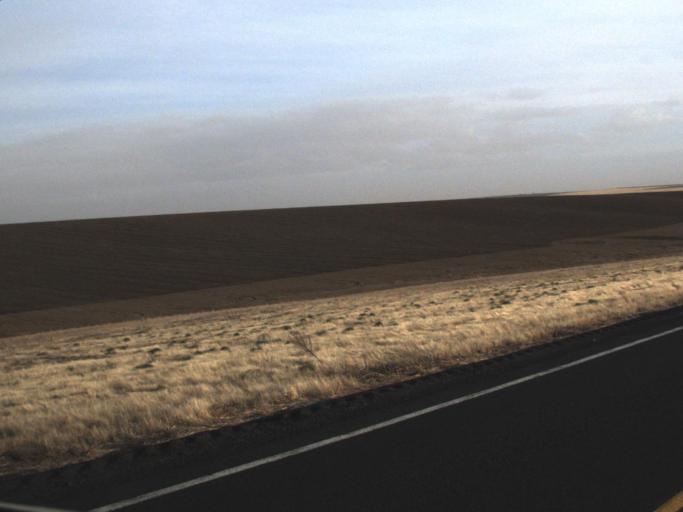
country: US
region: Washington
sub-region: Adams County
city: Ritzville
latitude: 47.1904
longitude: -118.6869
